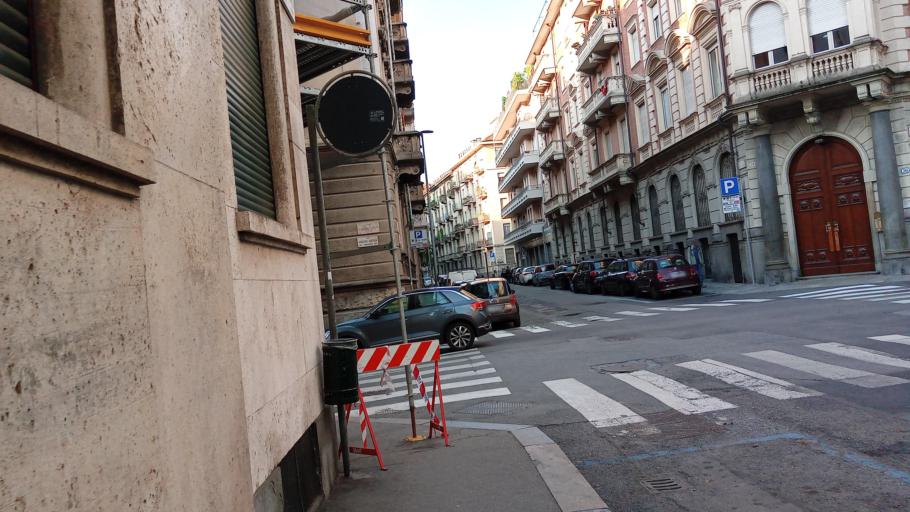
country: IT
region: Piedmont
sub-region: Provincia di Torino
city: Turin
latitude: 45.0557
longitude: 7.6800
